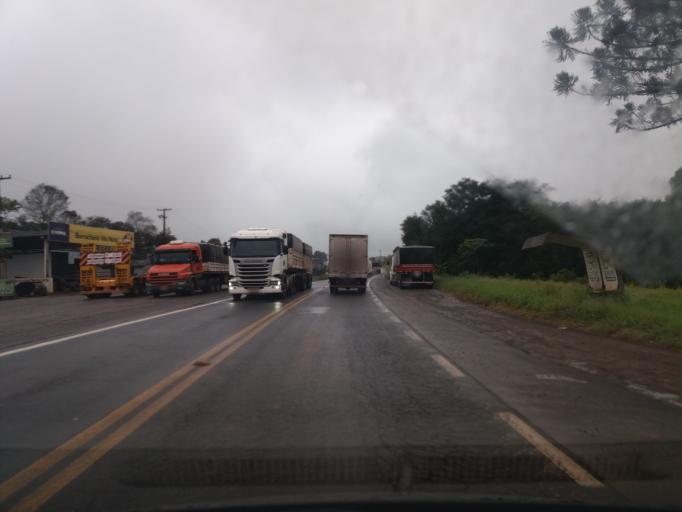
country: BR
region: Parana
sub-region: Realeza
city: Realeza
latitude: -25.4921
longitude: -53.5970
